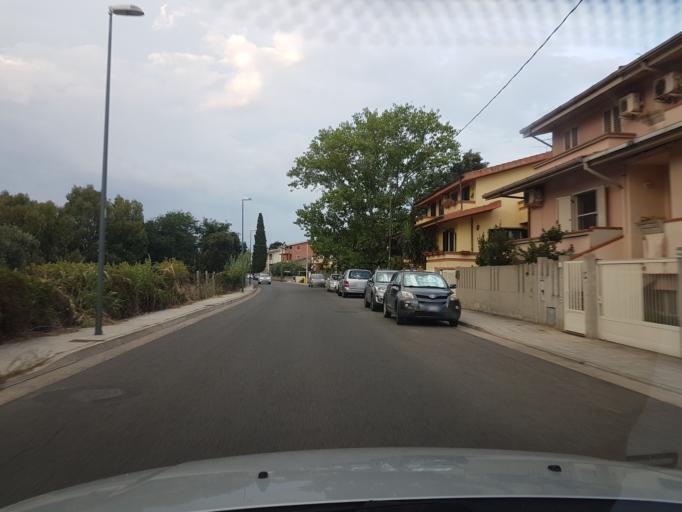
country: IT
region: Sardinia
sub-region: Provincia di Oristano
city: Donigala Fenugheddu
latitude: 39.9343
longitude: 8.5692
